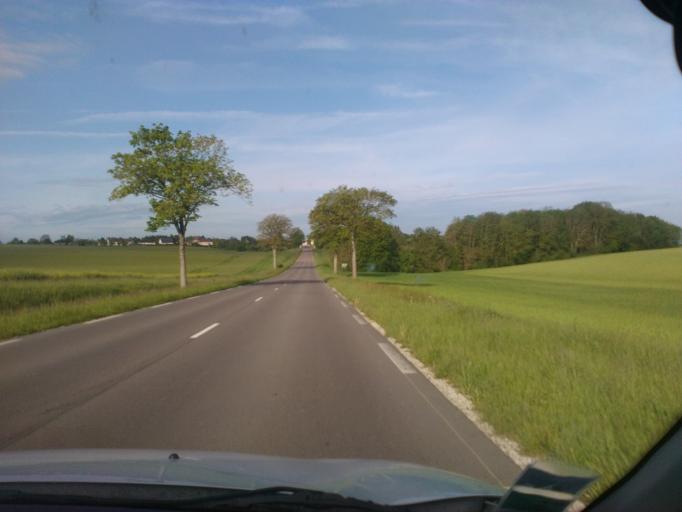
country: FR
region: Champagne-Ardenne
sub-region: Departement de l'Aube
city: Vendeuvre-sur-Barse
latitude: 48.2460
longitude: 4.5486
